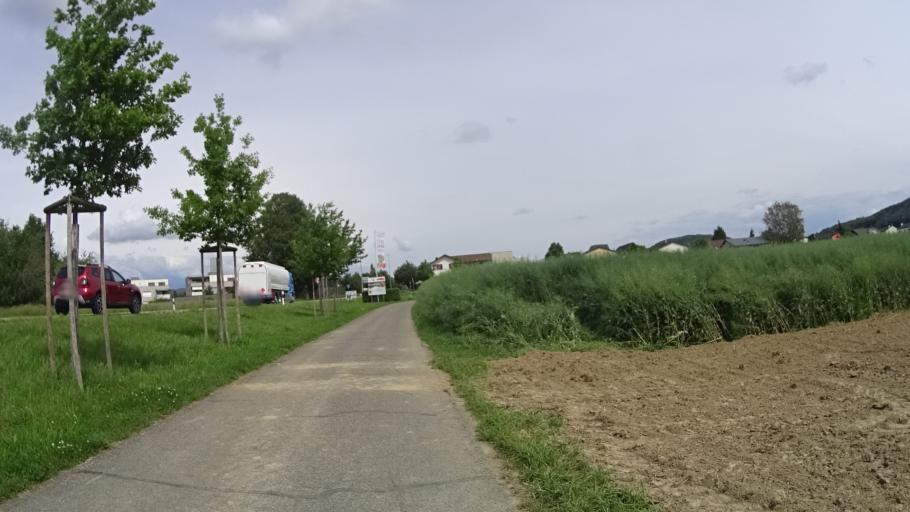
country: CH
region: Aargau
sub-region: Bezirk Rheinfelden
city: Mohlin
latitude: 47.5532
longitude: 7.8410
